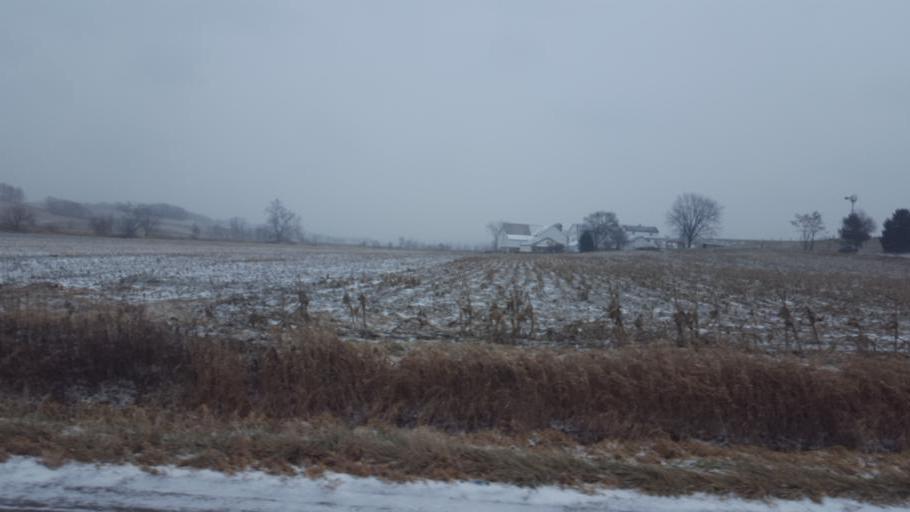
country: US
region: Ohio
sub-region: Tuscarawas County
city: Sugarcreek
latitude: 40.4673
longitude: -81.7276
